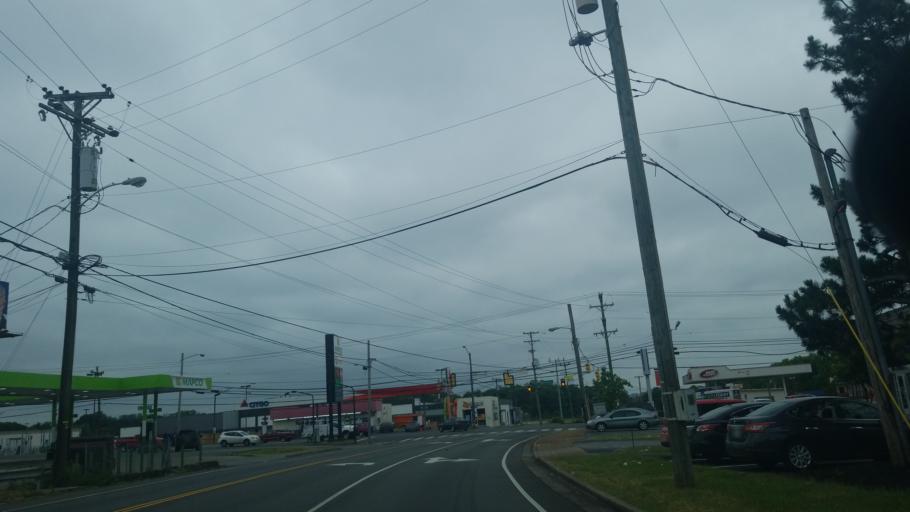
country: US
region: Tennessee
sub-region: Davidson County
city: Nashville
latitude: 36.2294
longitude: -86.7584
